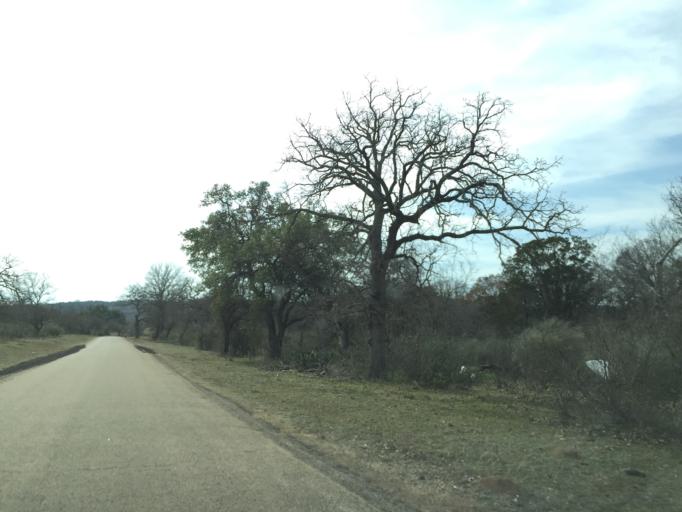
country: US
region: Texas
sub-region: Gillespie County
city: Fredericksburg
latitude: 30.4491
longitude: -98.6542
